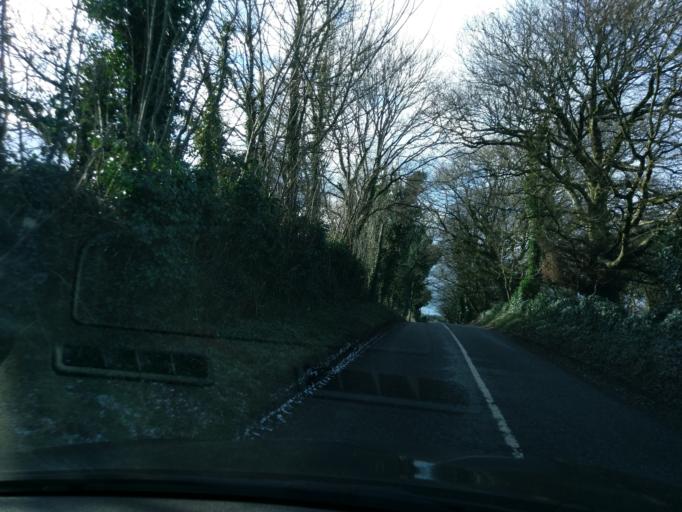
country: IE
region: Connaught
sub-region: County Galway
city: Athenry
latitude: 53.3879
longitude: -8.6044
